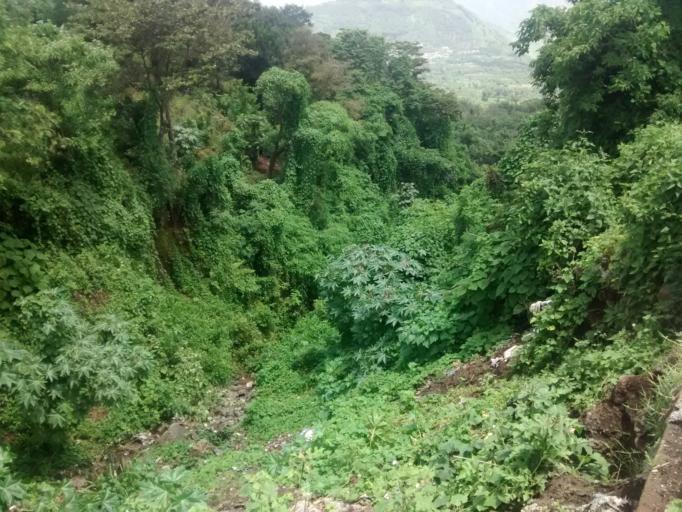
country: GT
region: Escuintla
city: San Vicente Pacaya
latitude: 14.4070
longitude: -90.6160
